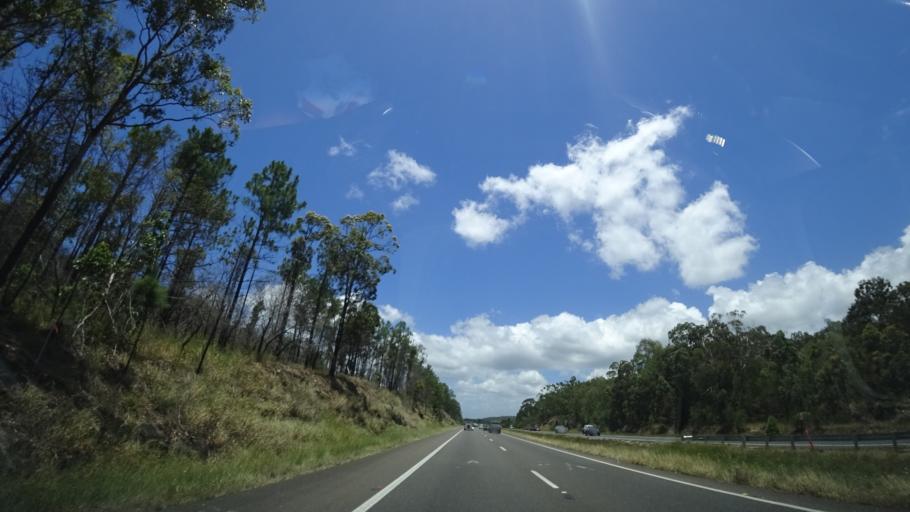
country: AU
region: Queensland
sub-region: Sunshine Coast
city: Little Mountain
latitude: -26.7953
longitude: 153.0443
